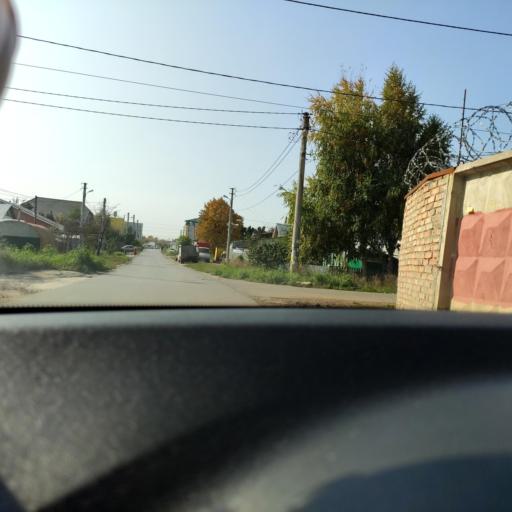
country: RU
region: Samara
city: Samara
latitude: 53.2313
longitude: 50.2312
